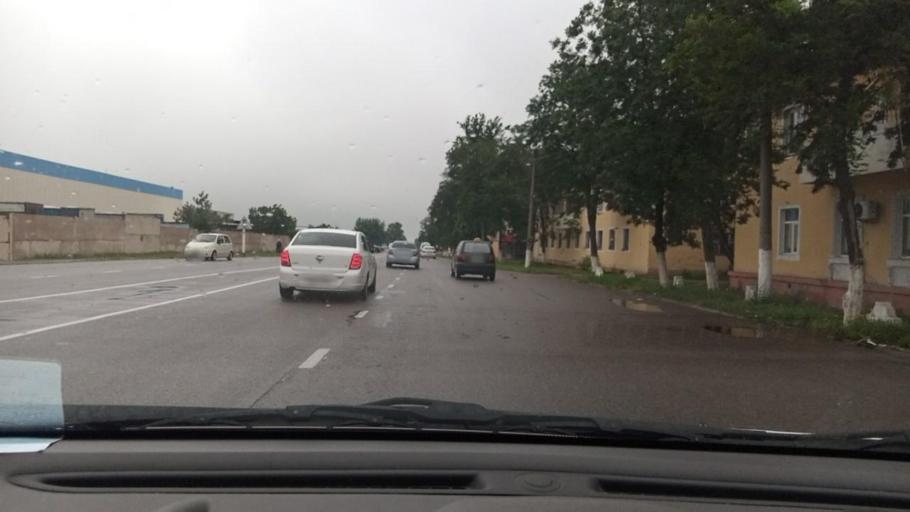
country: UZ
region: Toshkent
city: Angren
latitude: 41.0064
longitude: 70.0893
